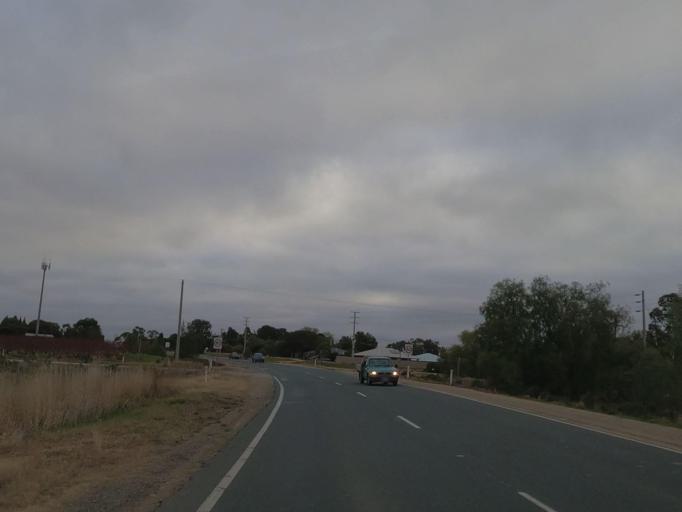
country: AU
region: Victoria
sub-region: Swan Hill
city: Swan Hill
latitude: -35.4670
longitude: 143.6563
